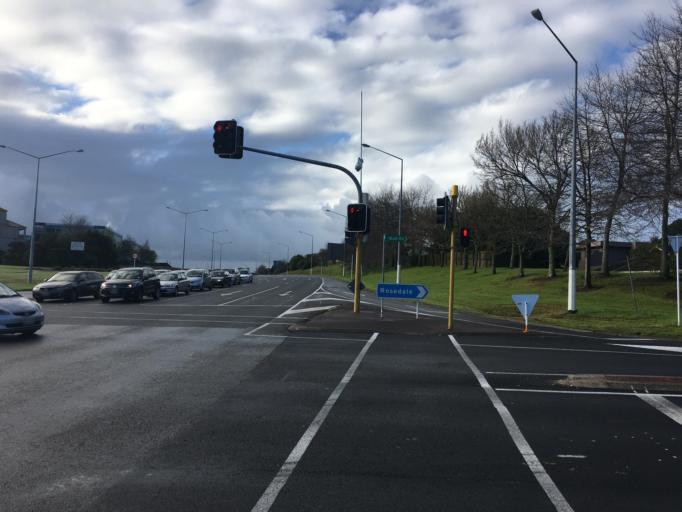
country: NZ
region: Auckland
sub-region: Auckland
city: Rothesay Bay
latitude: -36.7337
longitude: 174.7077
